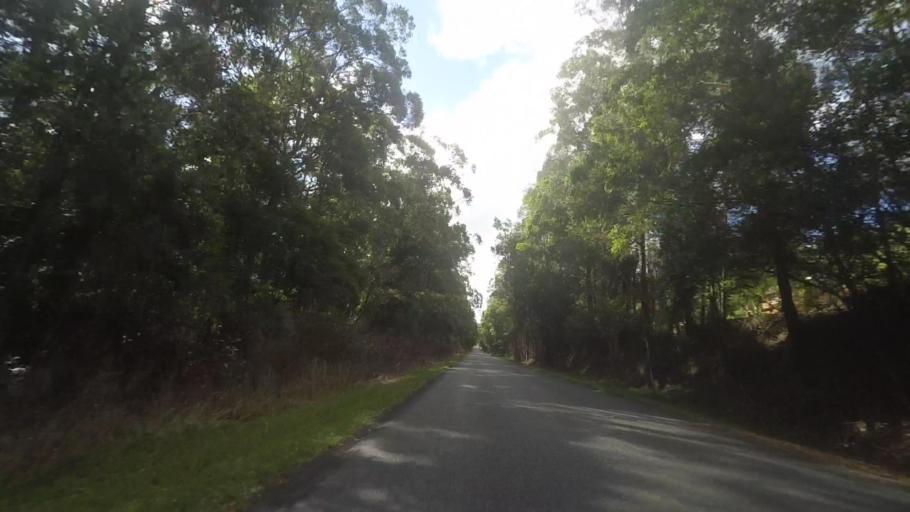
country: AU
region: New South Wales
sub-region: Great Lakes
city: Forster
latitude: -32.3937
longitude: 152.4550
